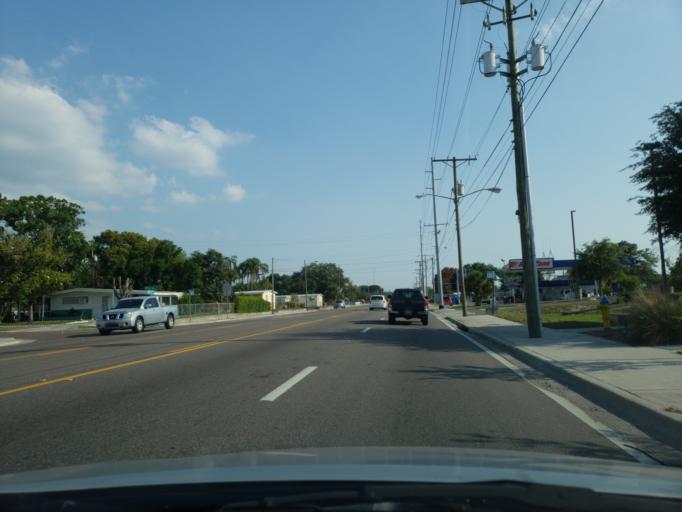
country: US
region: Florida
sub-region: Hillsborough County
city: Palm River-Clair Mel
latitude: 27.9363
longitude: -82.3687
